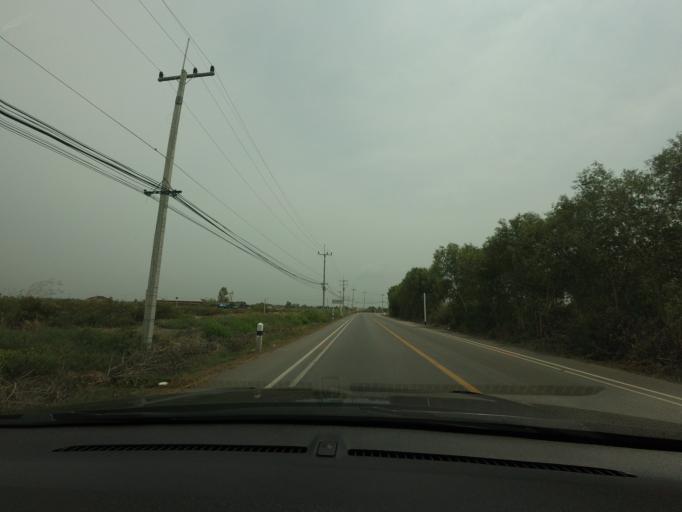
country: TH
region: Ratchaburi
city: Pak Tho
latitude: 13.3213
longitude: 99.9243
